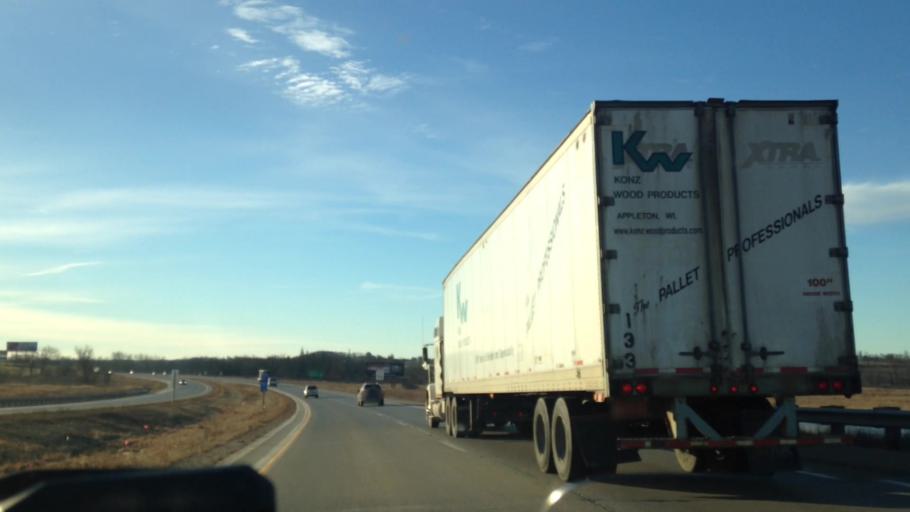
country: US
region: Wisconsin
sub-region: Dodge County
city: Theresa
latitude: 43.4638
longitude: -88.3669
